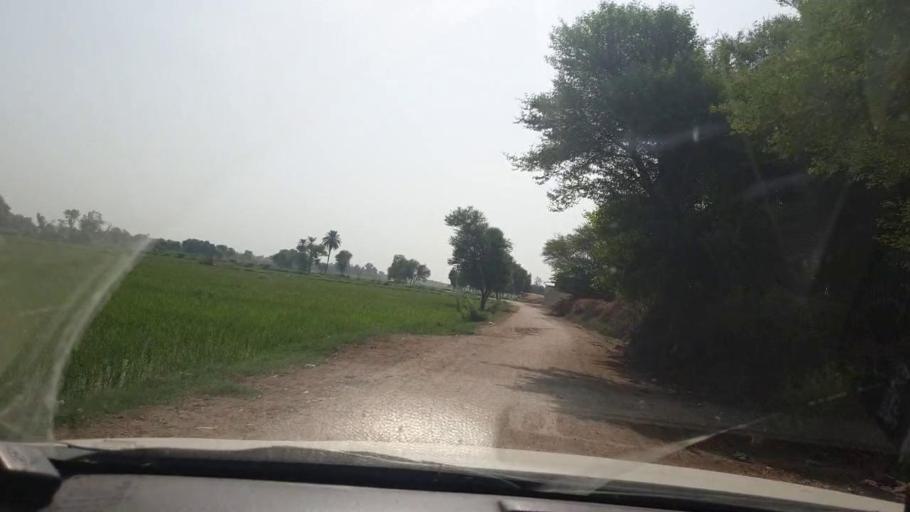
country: PK
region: Sindh
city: Chak
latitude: 27.8238
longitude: 68.7841
